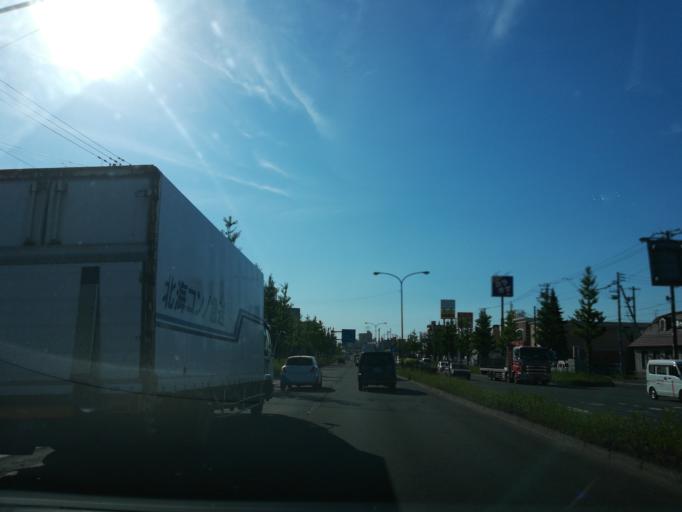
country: JP
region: Hokkaido
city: Kitahiroshima
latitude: 43.0225
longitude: 141.4714
